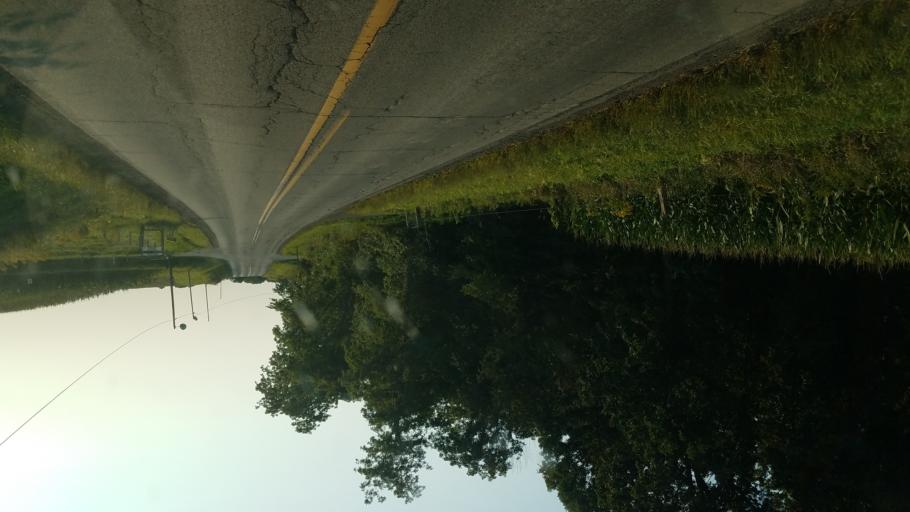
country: US
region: Ohio
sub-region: Wayne County
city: Apple Creek
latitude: 40.7026
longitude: -81.8417
